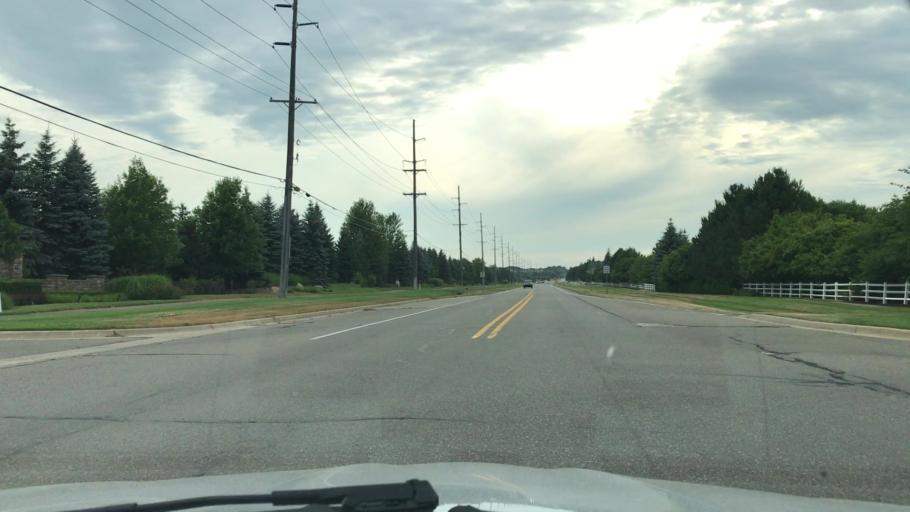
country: US
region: Michigan
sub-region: Wayne County
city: Northville
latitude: 42.4080
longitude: -83.5219
